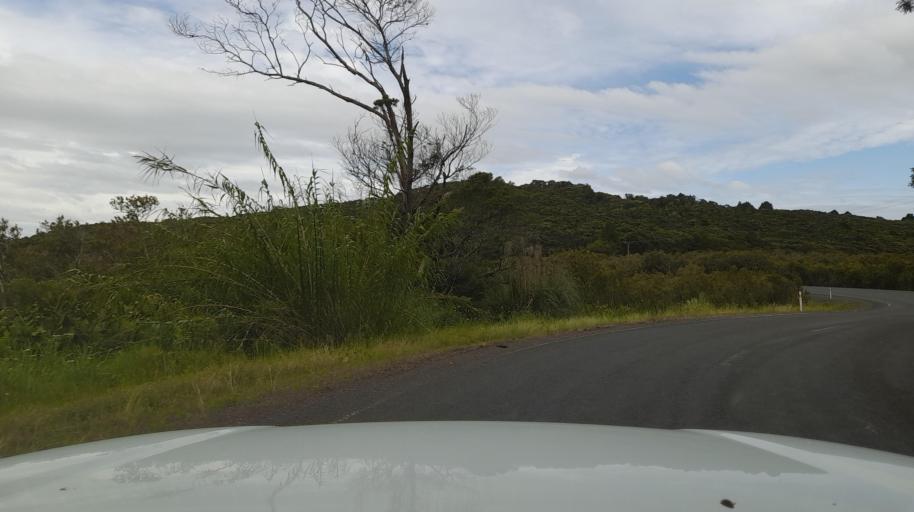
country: NZ
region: Northland
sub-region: Far North District
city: Kaitaia
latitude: -35.3934
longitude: 173.3806
